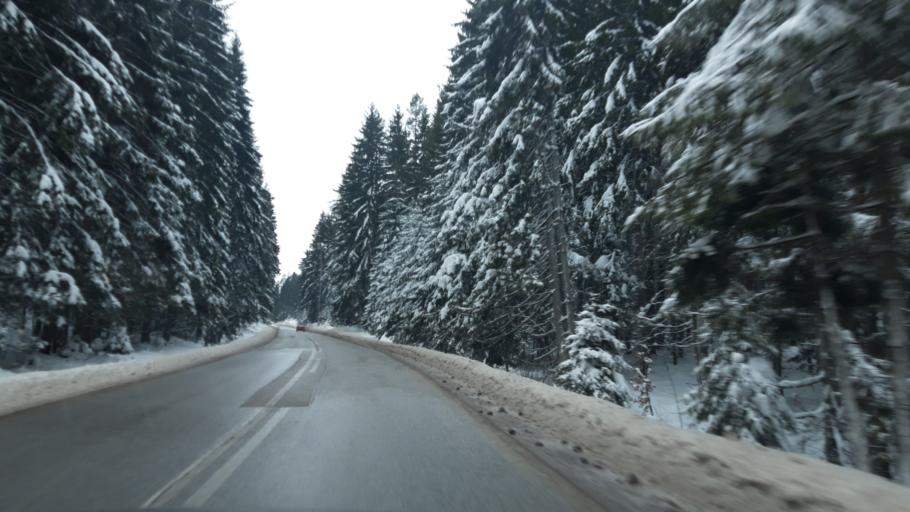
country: BA
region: Republika Srpska
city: Pale
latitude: 43.9249
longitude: 18.6561
